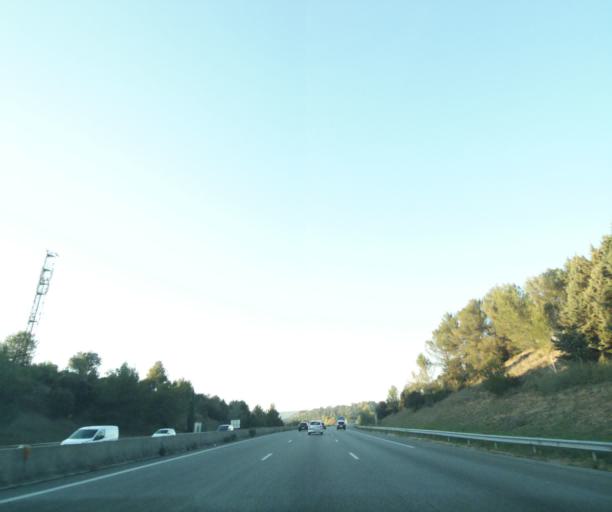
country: FR
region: Provence-Alpes-Cote d'Azur
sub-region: Departement des Bouches-du-Rhone
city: Meyreuil
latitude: 43.4888
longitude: 5.5293
